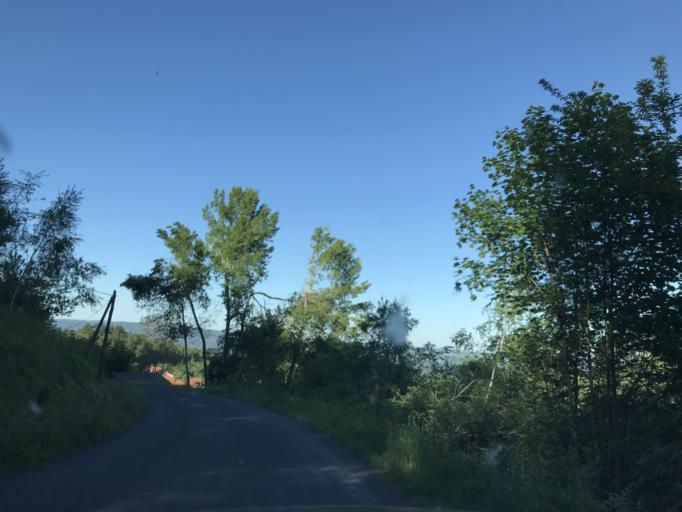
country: FR
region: Auvergne
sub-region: Departement du Puy-de-Dome
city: Job
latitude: 45.6963
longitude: 3.6841
